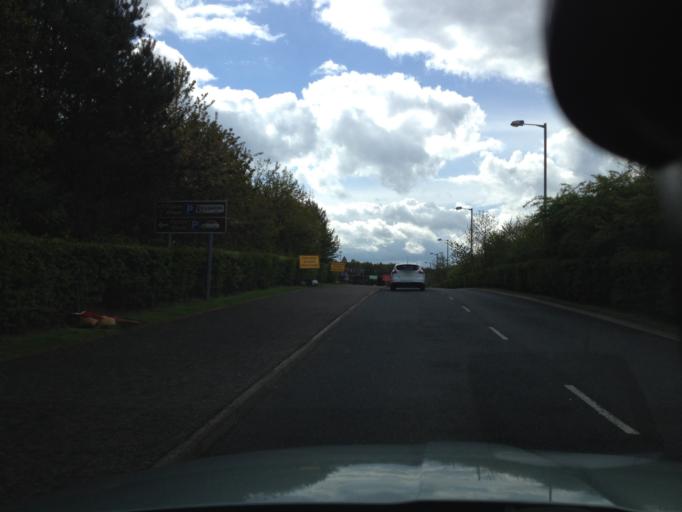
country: GB
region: Scotland
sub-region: Falkirk
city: Larbert
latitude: 56.0046
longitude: -3.8389
